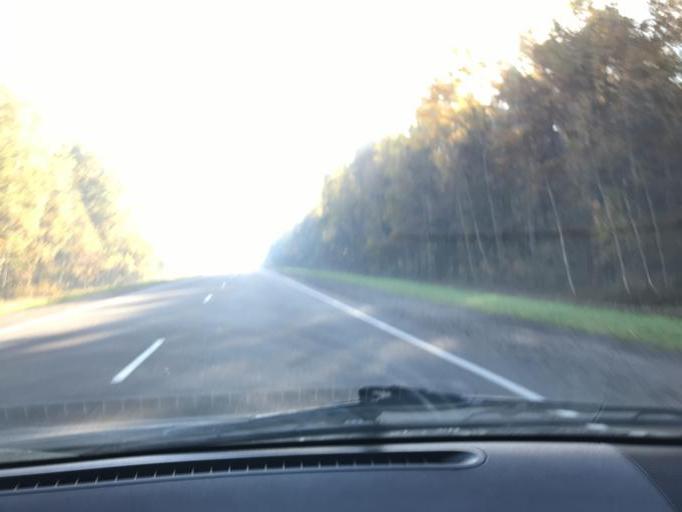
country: BY
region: Brest
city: Horad Luninyets
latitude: 52.3050
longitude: 26.6992
